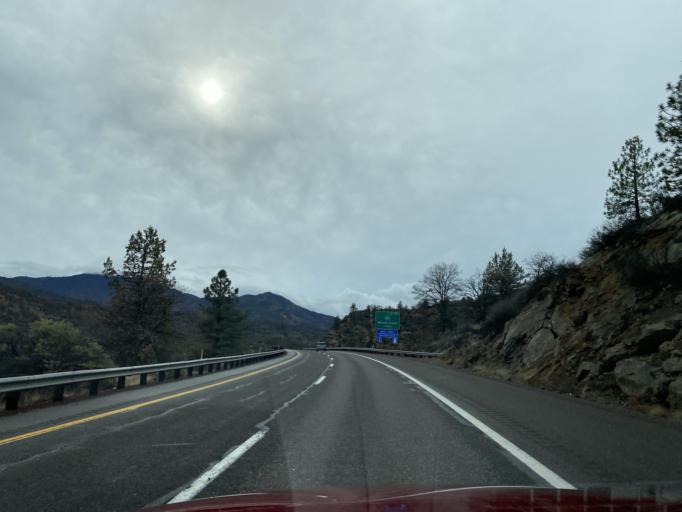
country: US
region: California
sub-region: Siskiyou County
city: Montague
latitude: 41.8766
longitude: -122.5600
